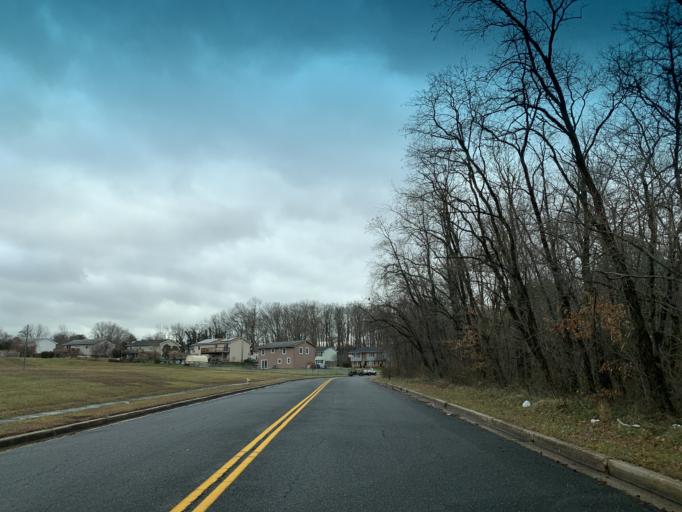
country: US
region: Maryland
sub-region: Harford County
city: Edgewood
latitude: 39.4290
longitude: -76.3162
